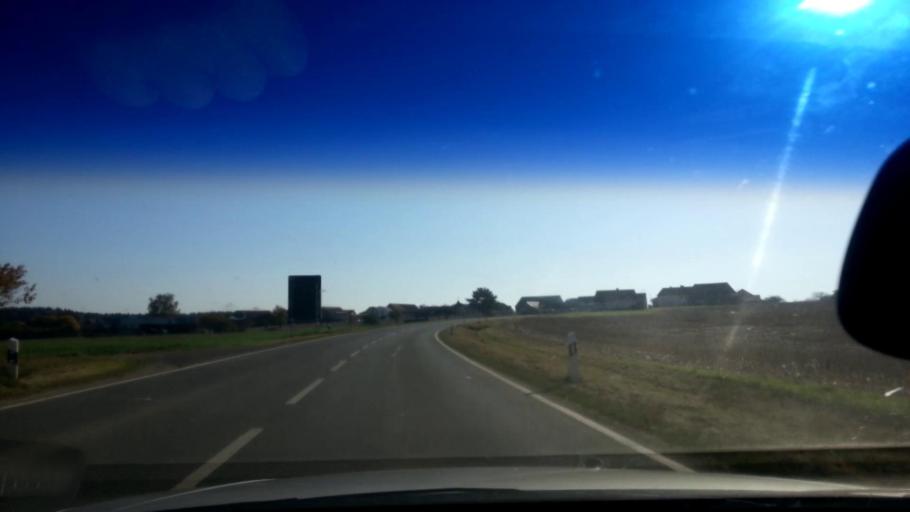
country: DE
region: Bavaria
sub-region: Upper Franconia
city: Stadelhofen
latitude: 49.9985
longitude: 11.2116
